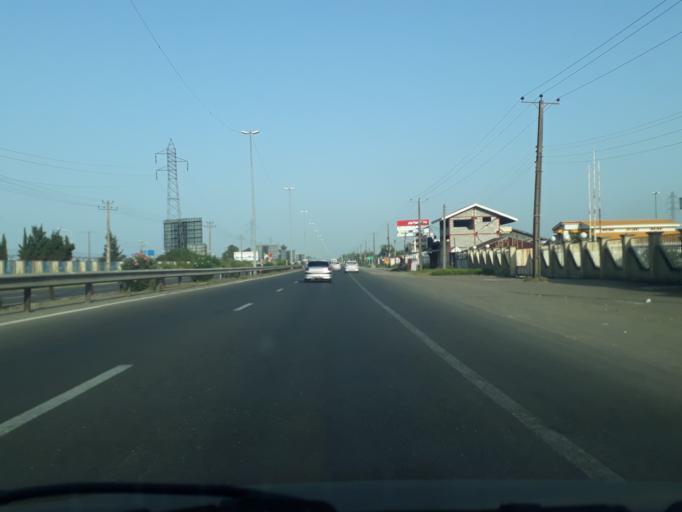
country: IR
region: Gilan
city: Bandar-e Anzali
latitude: 37.4600
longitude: 49.5895
